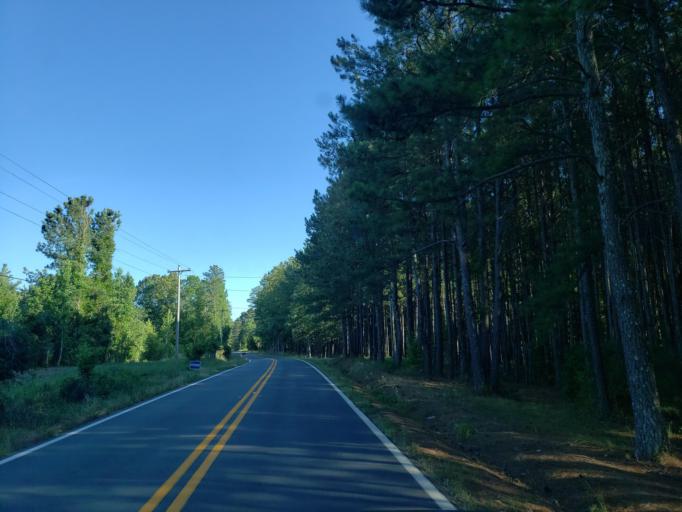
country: US
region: Georgia
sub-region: Floyd County
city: Shannon
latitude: 34.4550
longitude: -85.1150
